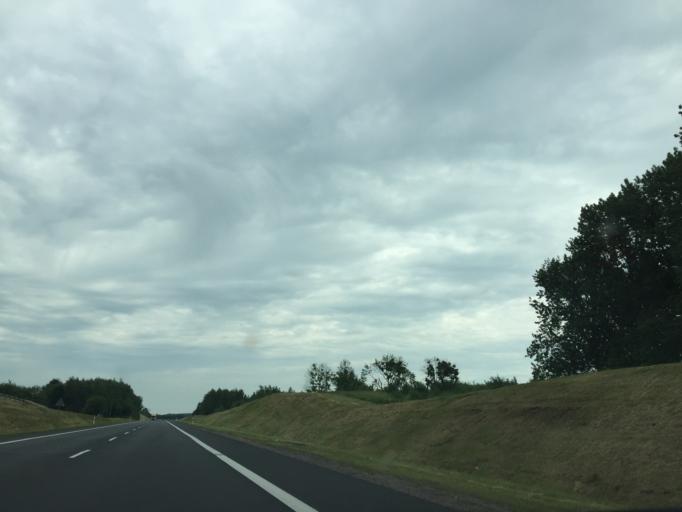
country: PL
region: Warmian-Masurian Voivodeship
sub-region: Powiat olsztynski
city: Biskupiec
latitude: 53.8307
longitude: 20.8948
